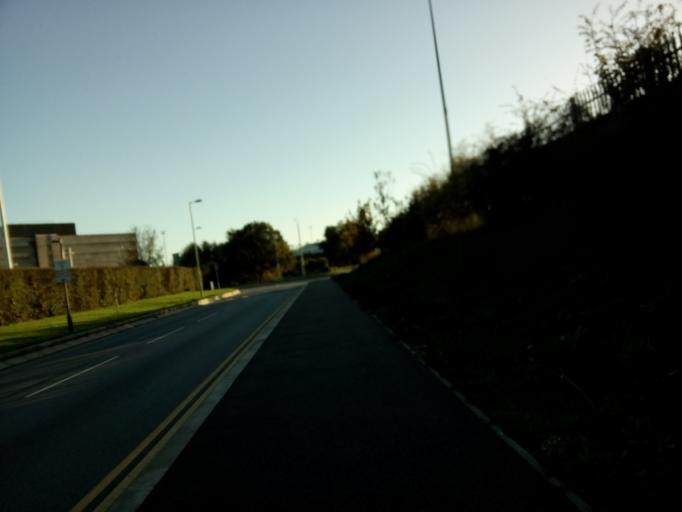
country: GB
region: England
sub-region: Suffolk
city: Felixstowe
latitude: 51.9663
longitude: 1.3178
